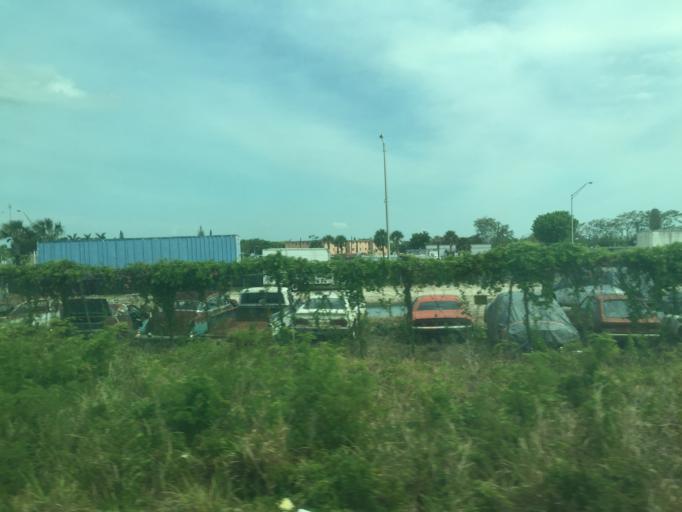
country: US
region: Florida
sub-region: Miami-Dade County
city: Opa-locka
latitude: 25.9051
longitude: -80.2425
